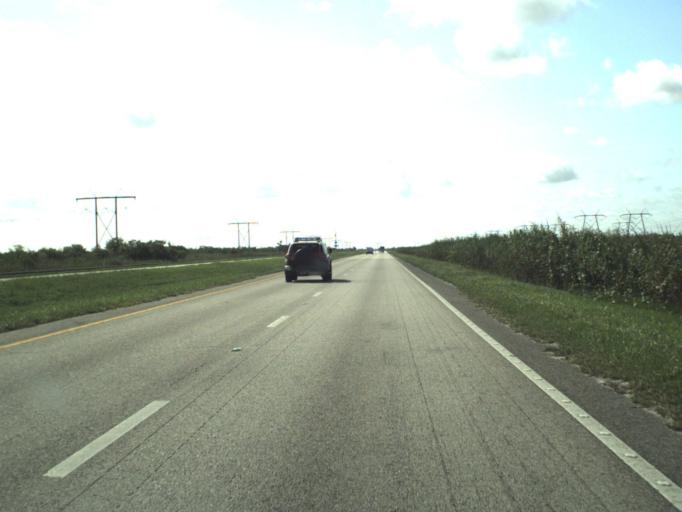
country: US
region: Florida
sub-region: Broward County
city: Weston
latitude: 26.2629
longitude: -80.4824
